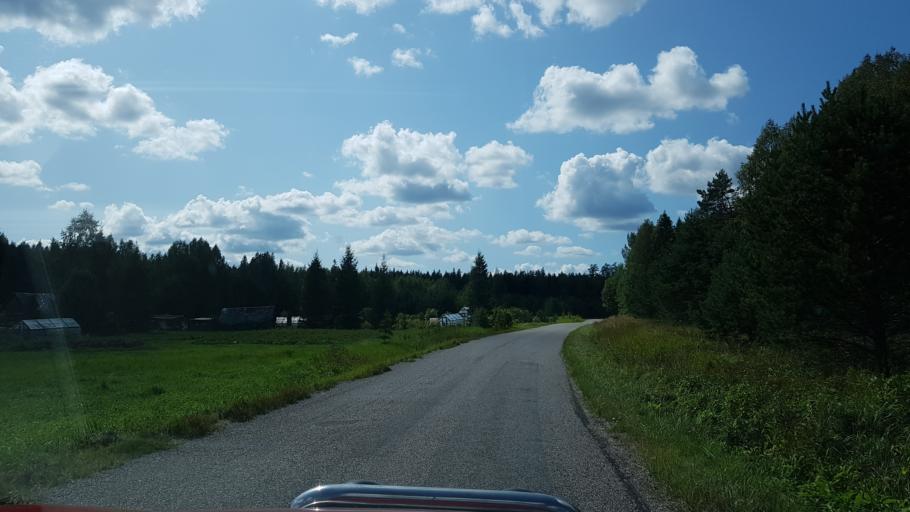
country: EE
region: Vorumaa
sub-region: Voru linn
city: Voru
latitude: 57.7208
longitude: 27.2071
